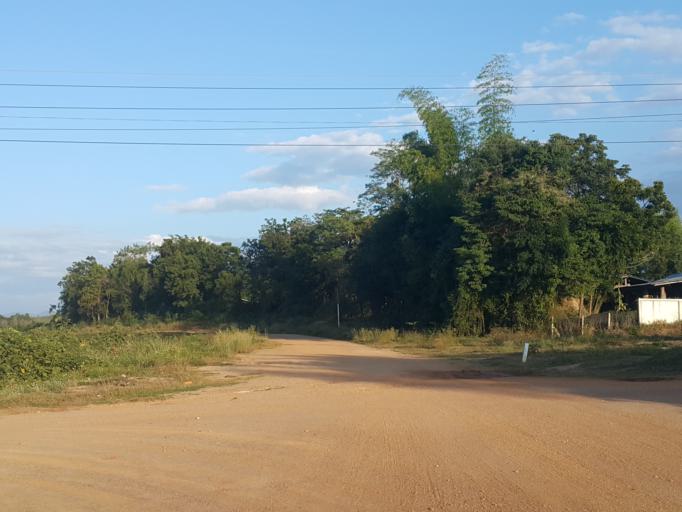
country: TH
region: Lampang
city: Lampang
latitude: 18.4252
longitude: 99.5727
